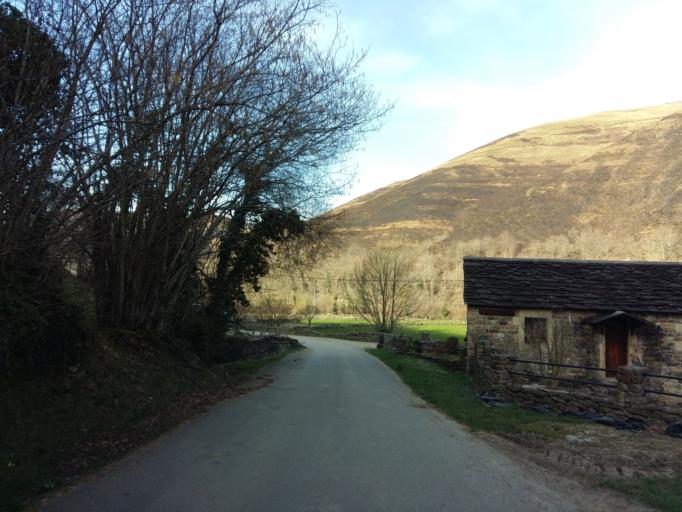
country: ES
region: Cantabria
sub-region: Provincia de Cantabria
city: Vega de Pas
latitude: 43.1427
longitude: -3.7969
